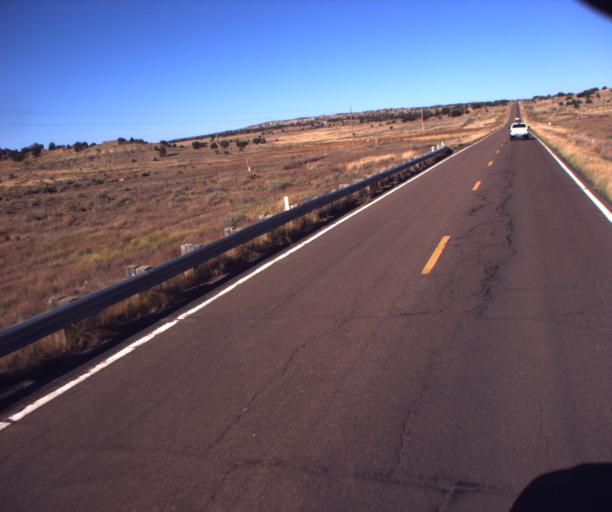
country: US
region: Arizona
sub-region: Apache County
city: Ganado
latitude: 35.7497
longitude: -109.8783
